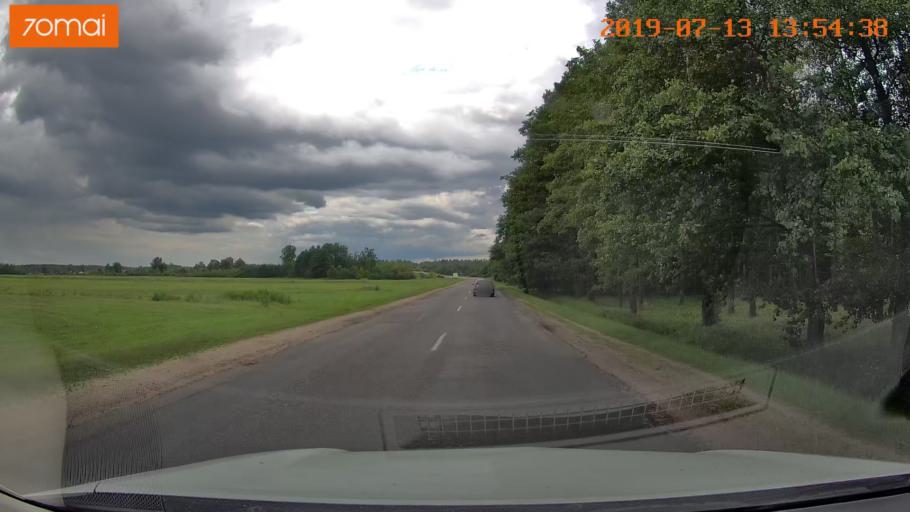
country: BY
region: Mogilev
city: Asipovichy
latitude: 53.2838
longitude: 28.6577
